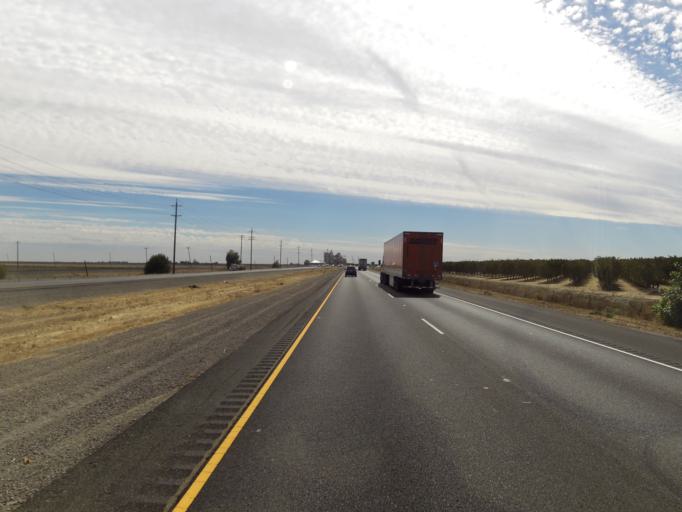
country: US
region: California
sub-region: Colusa County
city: Arbuckle
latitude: 39.0770
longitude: -122.0969
